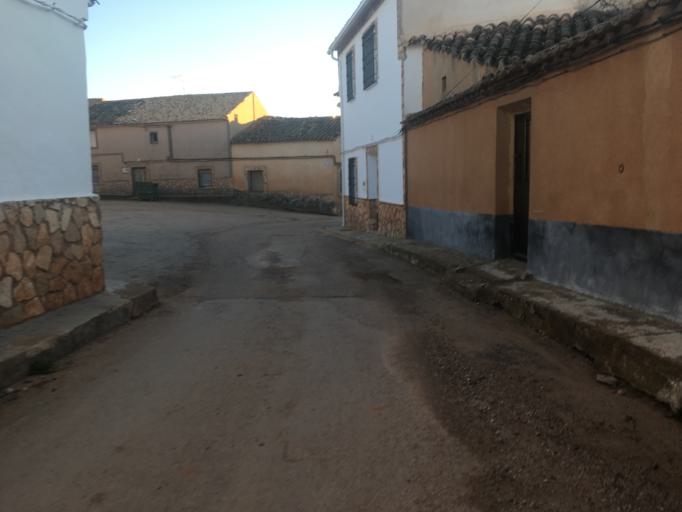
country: ES
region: Castille-La Mancha
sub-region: Provincia de Cuenca
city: Atalaya del Canavate
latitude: 39.5499
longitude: -2.2499
